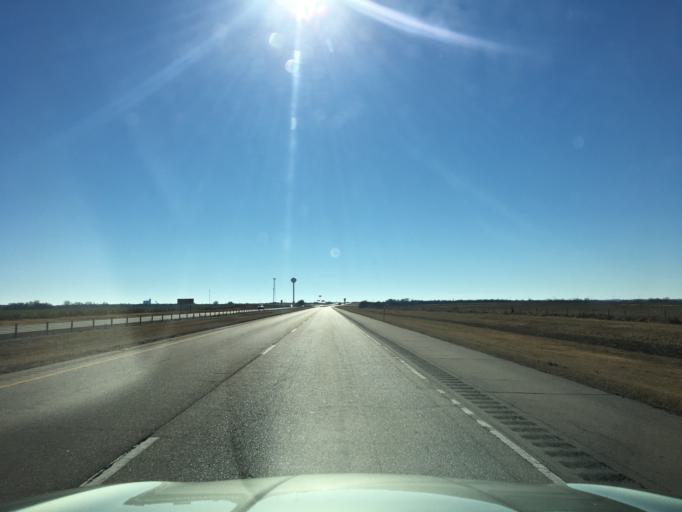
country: US
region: Oklahoma
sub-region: Kay County
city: Blackwell
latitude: 36.9537
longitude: -97.3458
